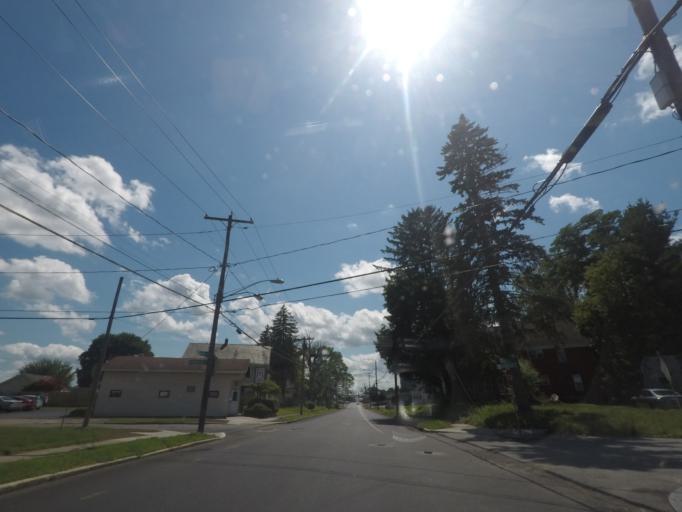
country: US
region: New York
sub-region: Schenectady County
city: Rotterdam
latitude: 42.7912
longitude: -73.9673
